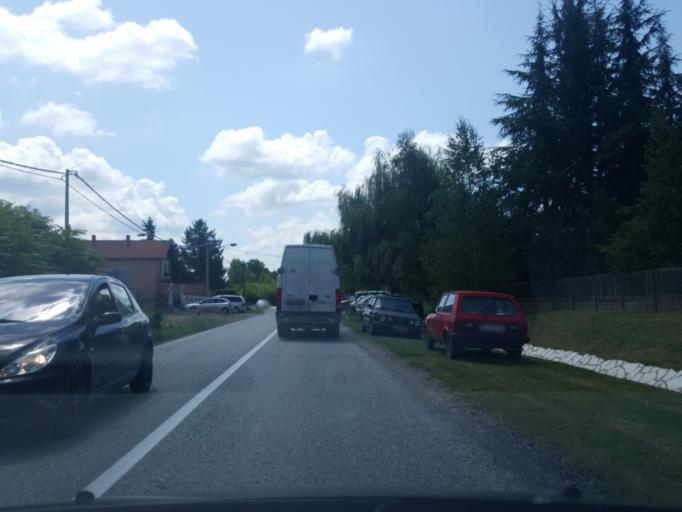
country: RS
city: Glusci
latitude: 44.8984
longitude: 19.5444
